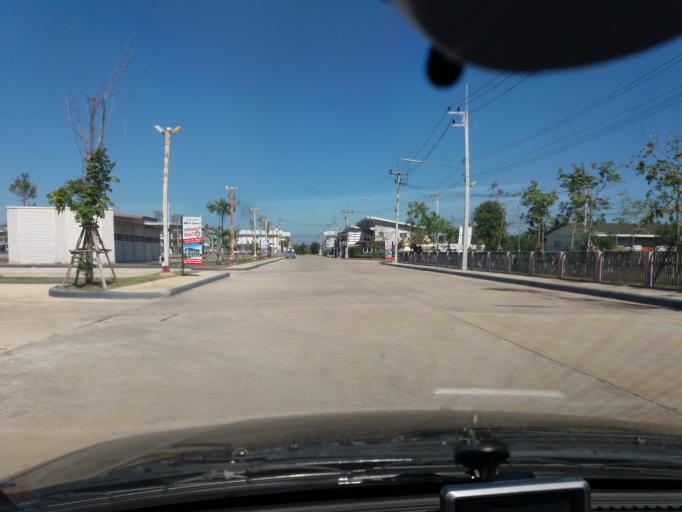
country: TH
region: Suphan Buri
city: Suphan Buri
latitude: 14.4594
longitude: 100.1459
